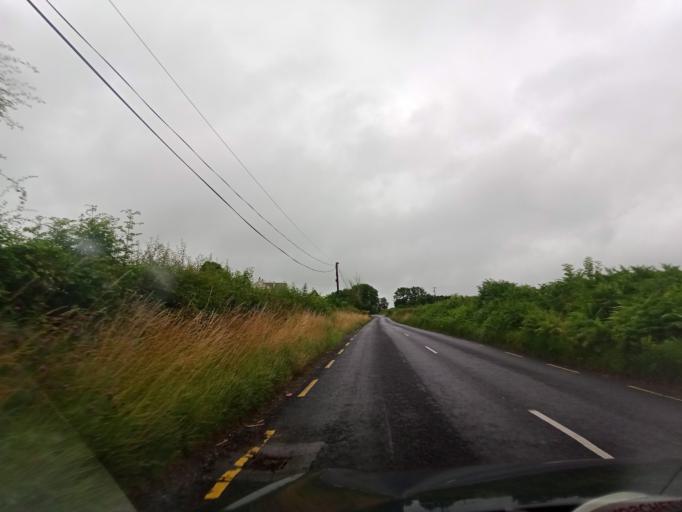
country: IE
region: Leinster
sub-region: Laois
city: Abbeyleix
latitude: 52.9101
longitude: -7.3097
